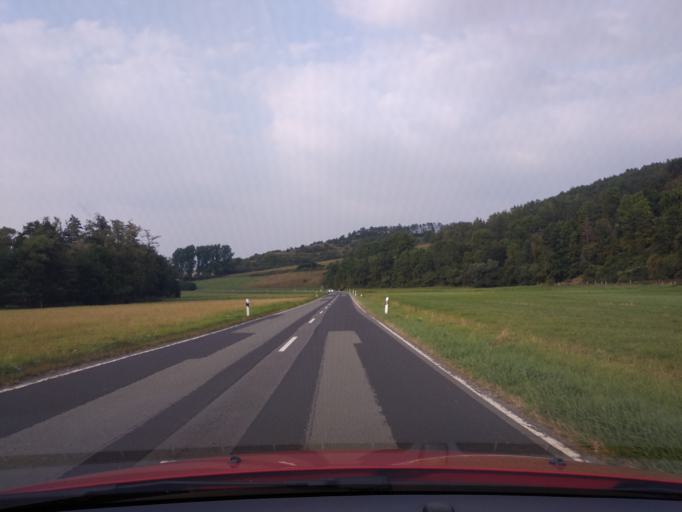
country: DE
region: Hesse
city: Liebenau
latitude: 51.4910
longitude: 9.2985
